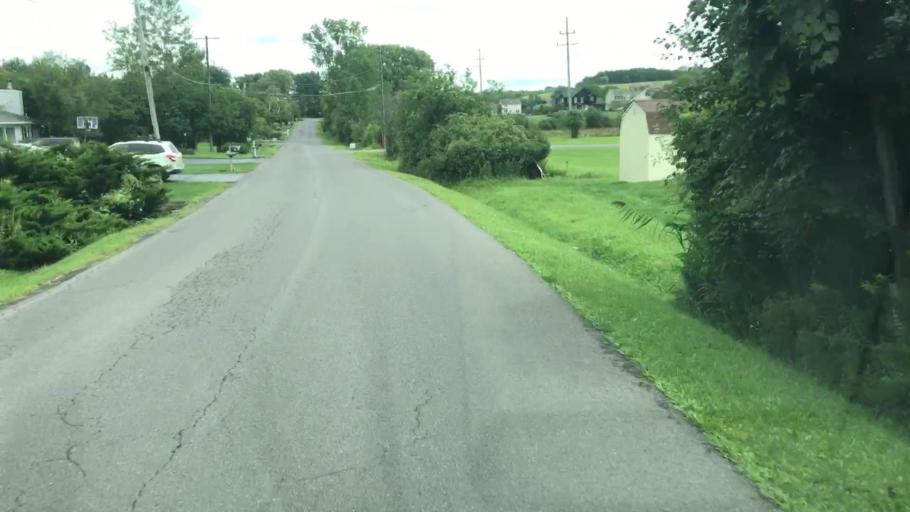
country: US
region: New York
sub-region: Cayuga County
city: Melrose Park
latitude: 42.9124
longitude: -76.5350
